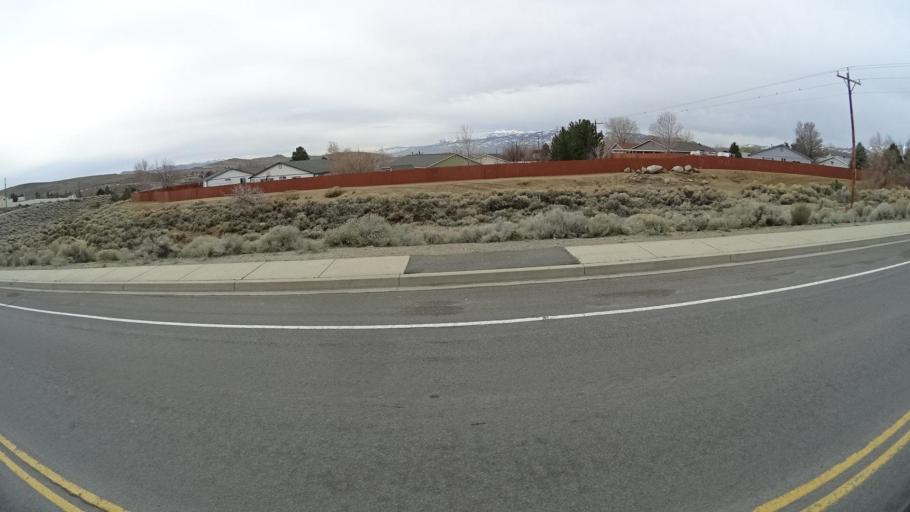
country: US
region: Nevada
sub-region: Washoe County
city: Sun Valley
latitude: 39.6135
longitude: -119.7628
